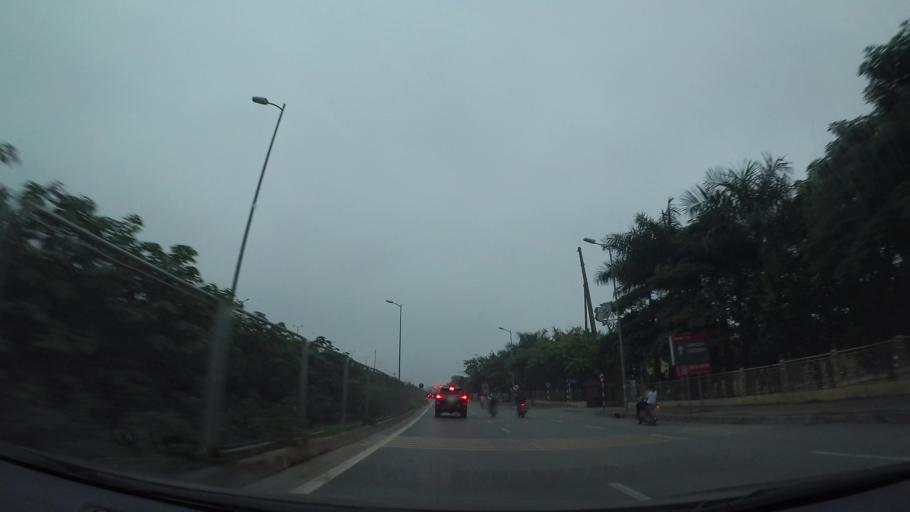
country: VN
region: Ha Noi
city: Van Dien
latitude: 20.9635
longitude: 105.8665
